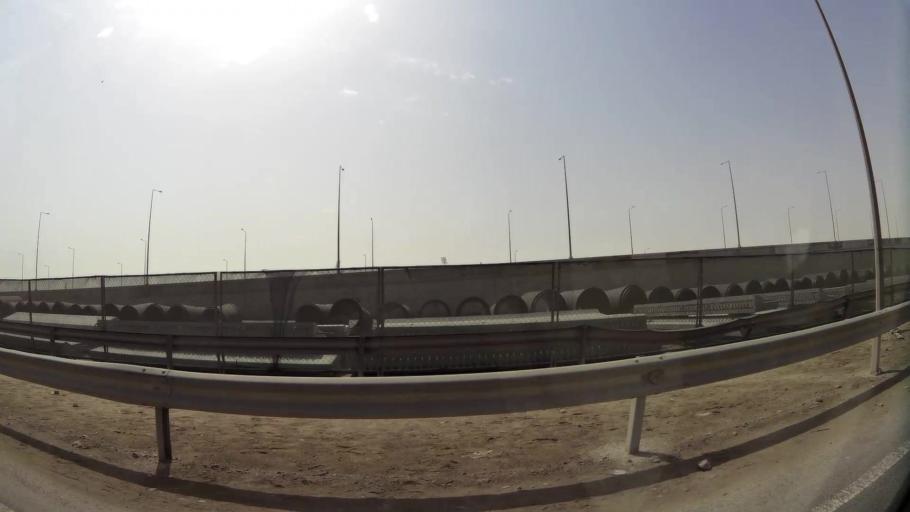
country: QA
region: Al Wakrah
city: Al Wukayr
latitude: 25.1941
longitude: 51.4573
